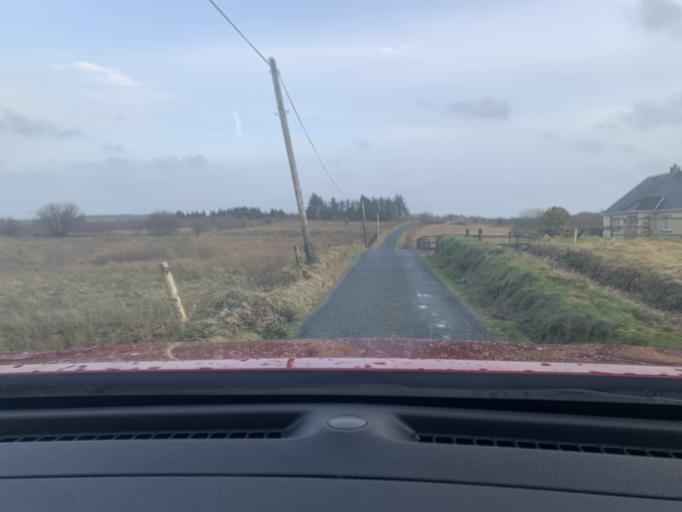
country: IE
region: Connaught
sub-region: Roscommon
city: Ballaghaderreen
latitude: 53.9585
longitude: -8.5382
